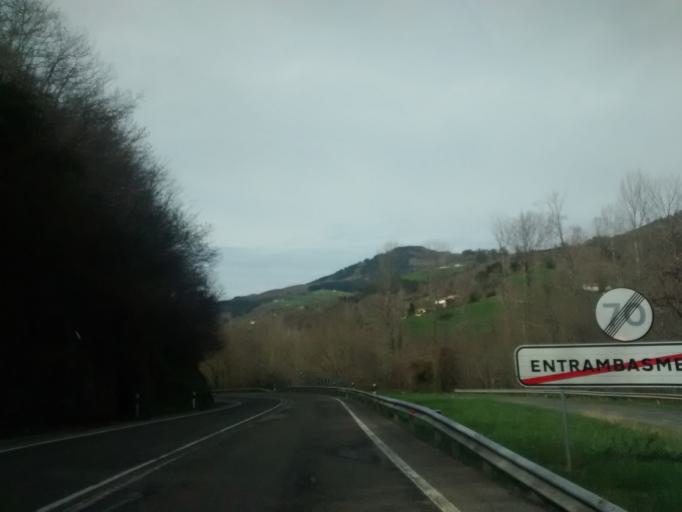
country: ES
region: Cantabria
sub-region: Provincia de Cantabria
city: Santiurde de Toranzo
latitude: 43.1720
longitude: -3.9006
